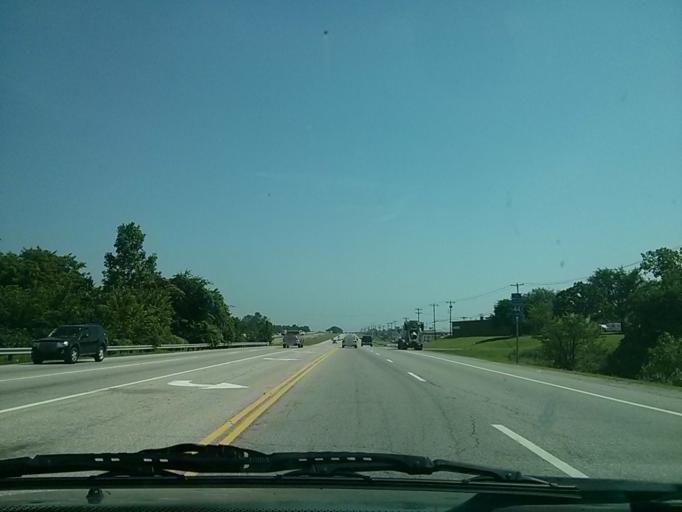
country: US
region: Oklahoma
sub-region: Tulsa County
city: Oakhurst
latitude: 36.0466
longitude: -96.0784
